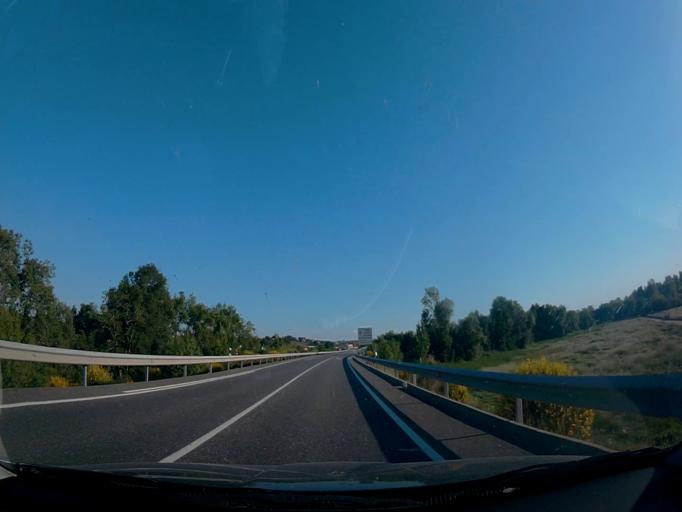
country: ES
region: Castille-La Mancha
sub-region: Province of Toledo
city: Escalona
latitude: 40.1636
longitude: -4.3979
